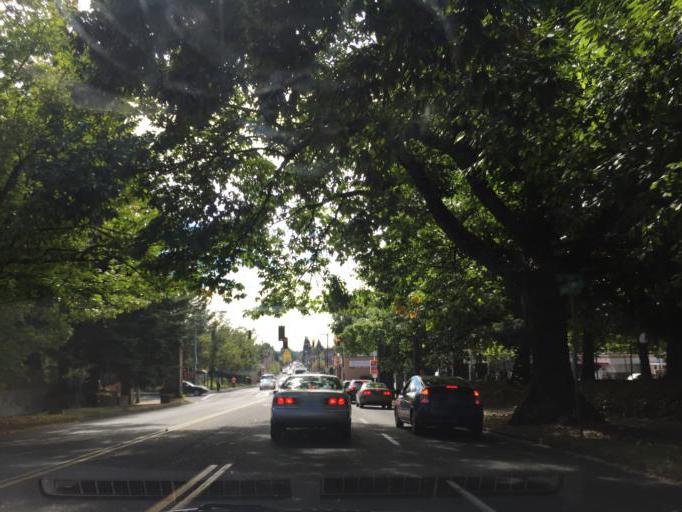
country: US
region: Oregon
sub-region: Multnomah County
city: Portland
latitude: 45.5199
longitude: -122.6231
